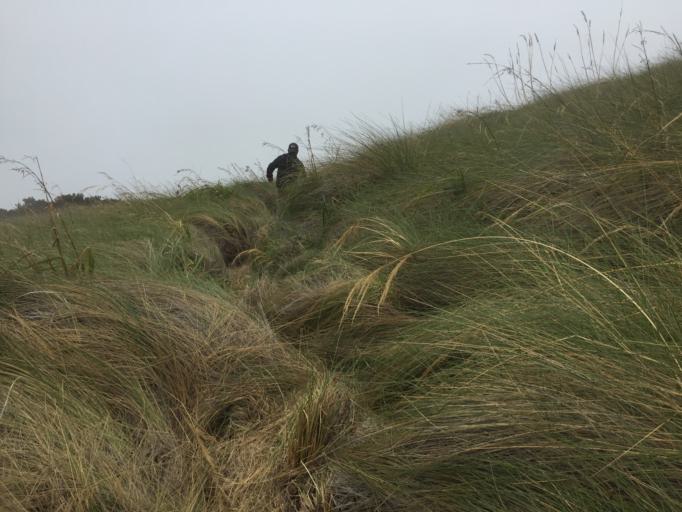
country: EC
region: Imbabura
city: Atuntaqui
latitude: 0.2798
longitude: -78.1814
